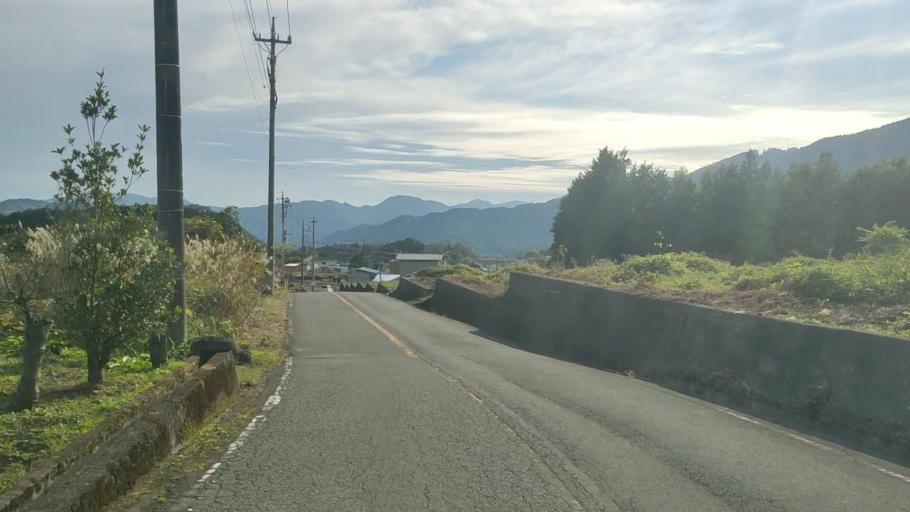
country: JP
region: Shizuoka
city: Fujinomiya
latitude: 35.2498
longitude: 138.5669
